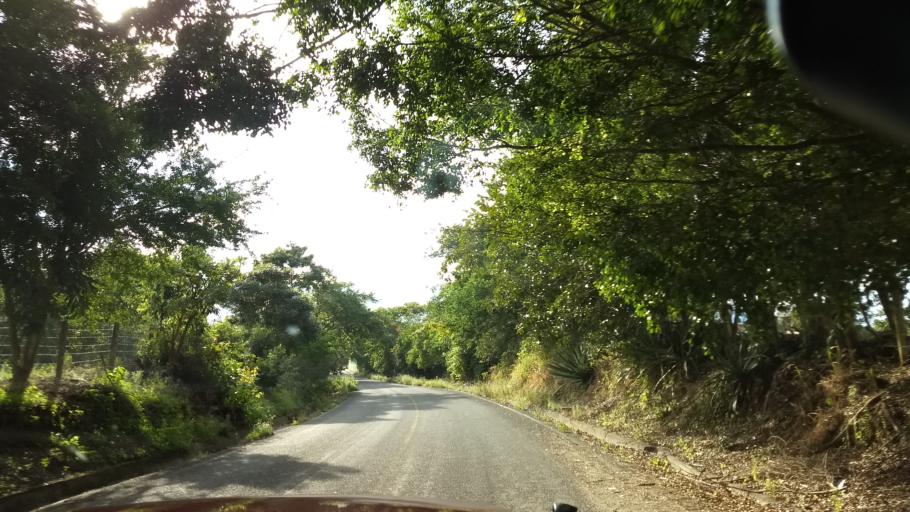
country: MX
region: Colima
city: Suchitlan
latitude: 19.4681
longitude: -103.7652
